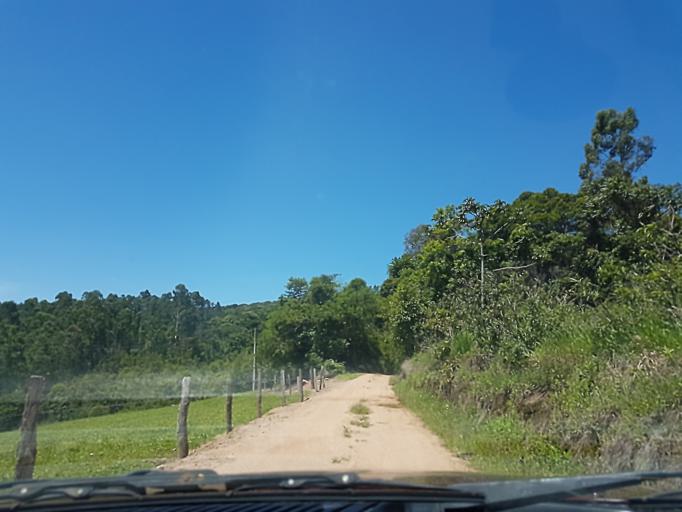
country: BR
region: Santa Catarina
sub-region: Braco Do Norte
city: Braco do Norte
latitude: -28.3876
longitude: -49.1263
